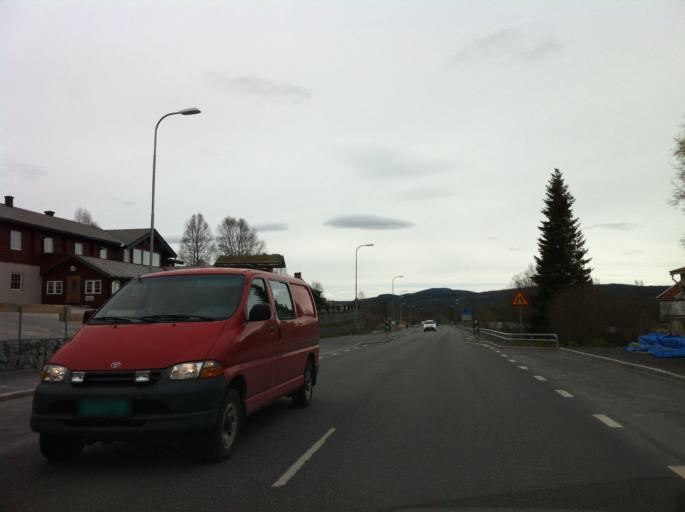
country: NO
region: Hedmark
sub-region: Engerdal
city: Engerdal
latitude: 62.5444
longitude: 12.5462
